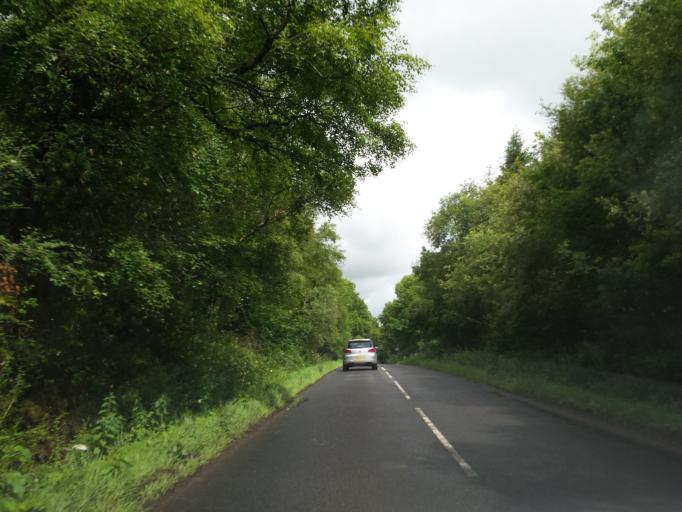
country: GB
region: Scotland
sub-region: Fife
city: Strathkinness
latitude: 56.3251
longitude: -2.8751
